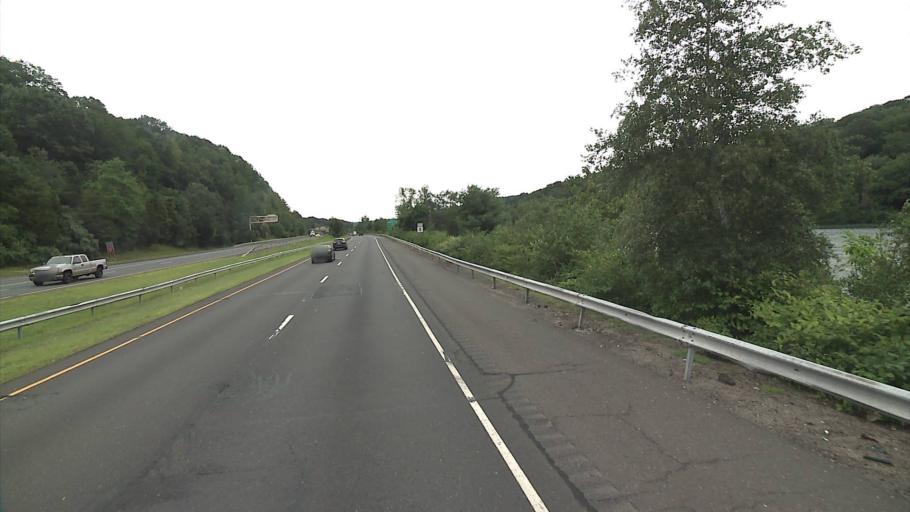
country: US
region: Connecticut
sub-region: New Haven County
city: Seymour
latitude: 41.3725
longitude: -73.0845
